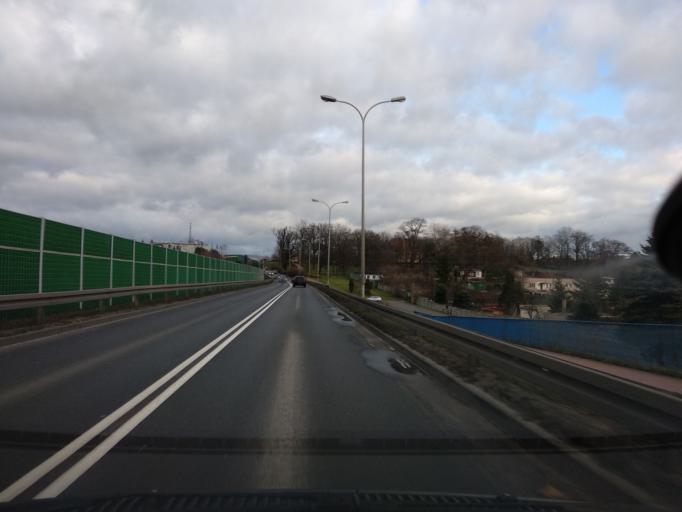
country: PL
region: Greater Poland Voivodeship
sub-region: Kalisz
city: Kalisz
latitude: 51.7734
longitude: 18.0748
